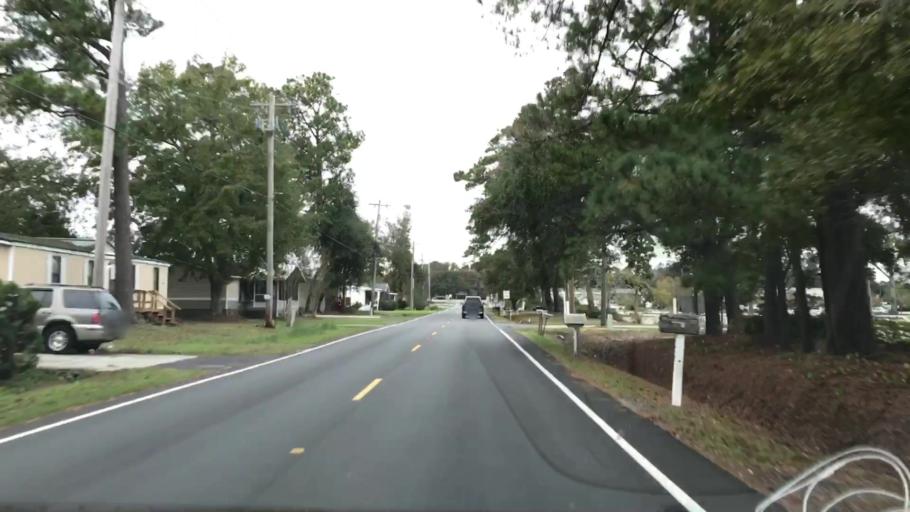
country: US
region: South Carolina
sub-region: Horry County
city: Garden City
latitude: 33.5884
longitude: -79.0039
